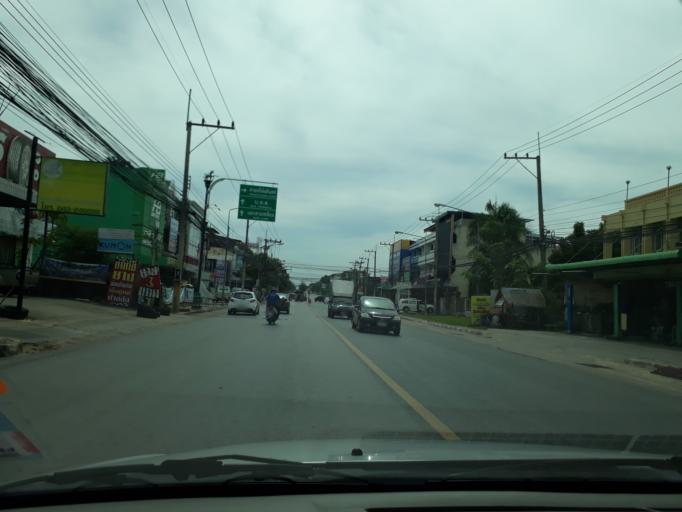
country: TH
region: Khon Kaen
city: Khon Kaen
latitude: 16.4378
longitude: 102.8411
